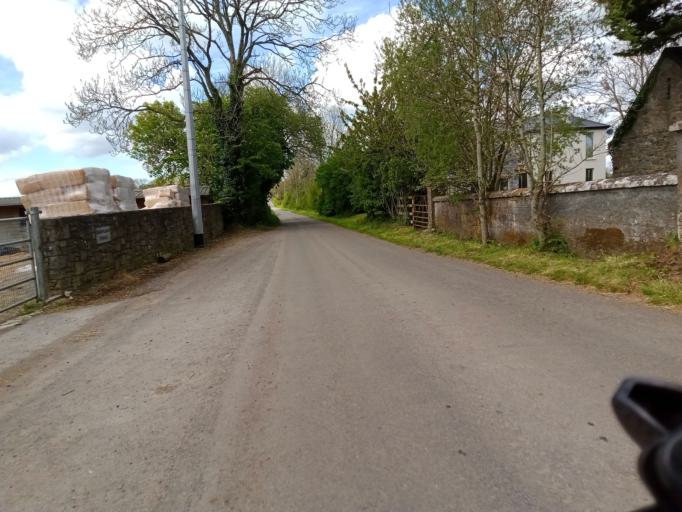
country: IE
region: Leinster
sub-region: Kilkenny
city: Thomastown
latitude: 52.5826
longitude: -7.1337
